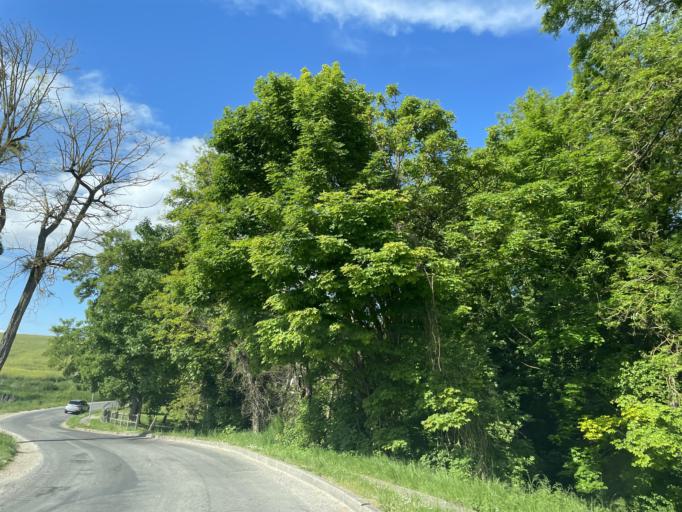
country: FR
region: Ile-de-France
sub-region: Departement de Seine-et-Marne
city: Charny
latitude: 48.9488
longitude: 2.7792
